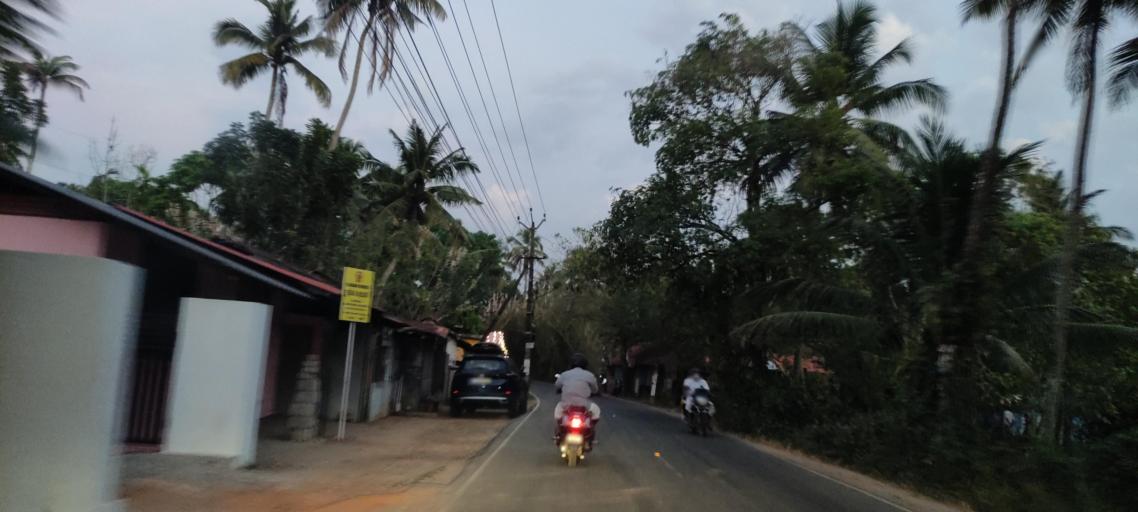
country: IN
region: Kerala
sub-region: Alappuzha
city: Kutiatodu
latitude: 9.7731
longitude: 76.3431
